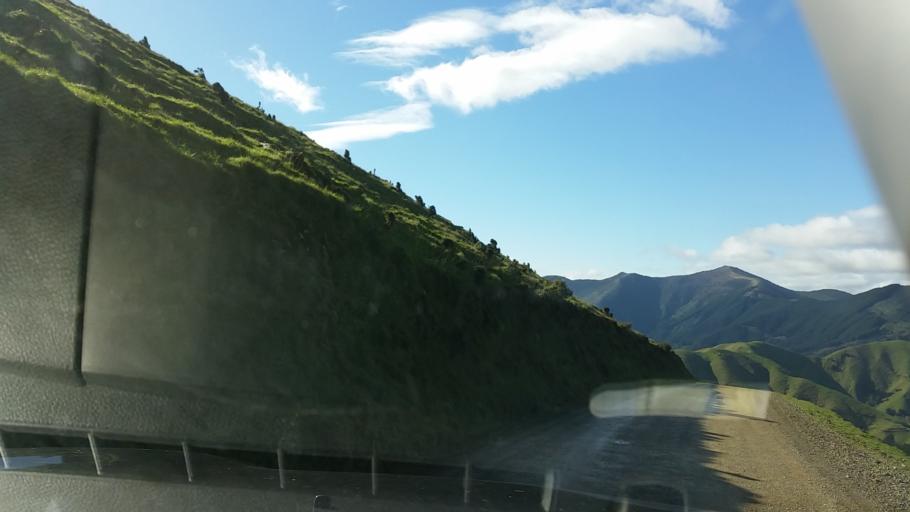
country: NZ
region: Marlborough
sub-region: Marlborough District
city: Picton
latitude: -40.9885
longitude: 173.8060
